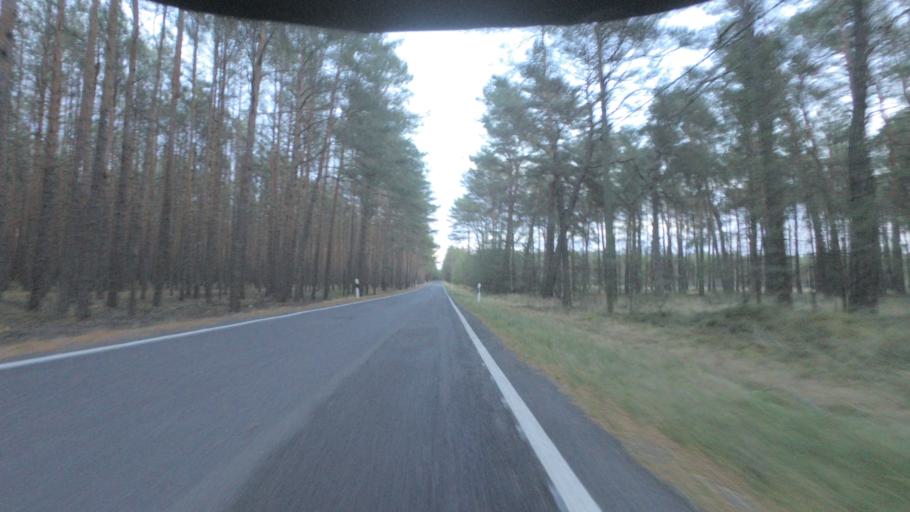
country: DE
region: Brandenburg
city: Schonewalde
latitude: 51.7563
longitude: 13.5972
